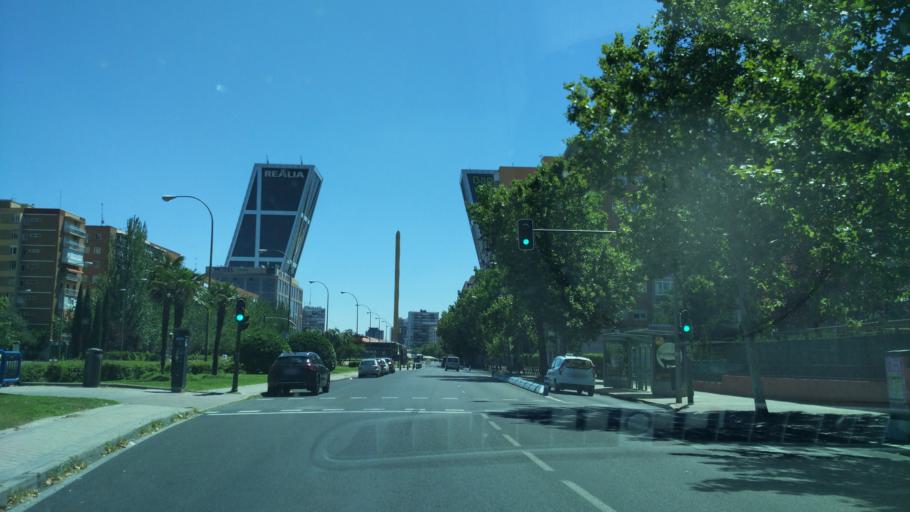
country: ES
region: Madrid
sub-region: Provincia de Madrid
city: Chamartin
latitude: 40.4712
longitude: -3.6882
